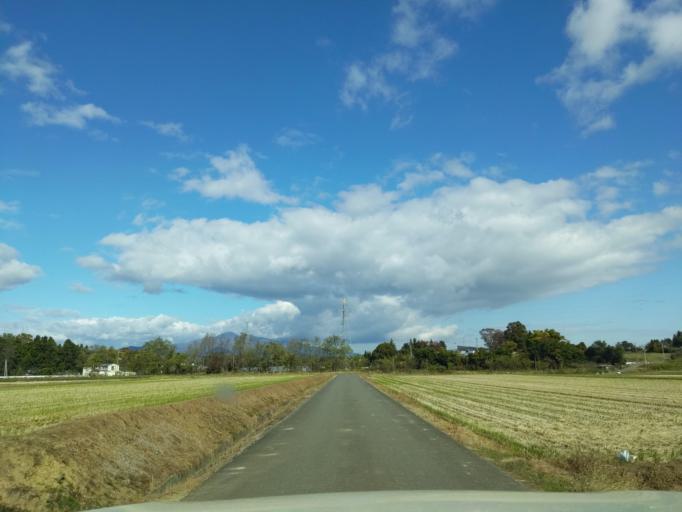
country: JP
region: Fukushima
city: Koriyama
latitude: 37.4275
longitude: 140.3289
